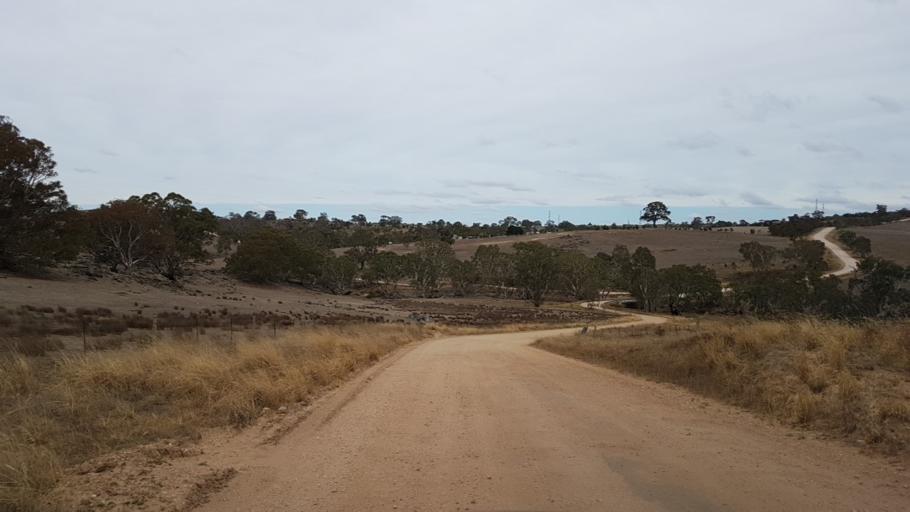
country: AU
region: South Australia
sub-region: Adelaide Hills
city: Birdwood
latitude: -34.8769
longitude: 139.0843
